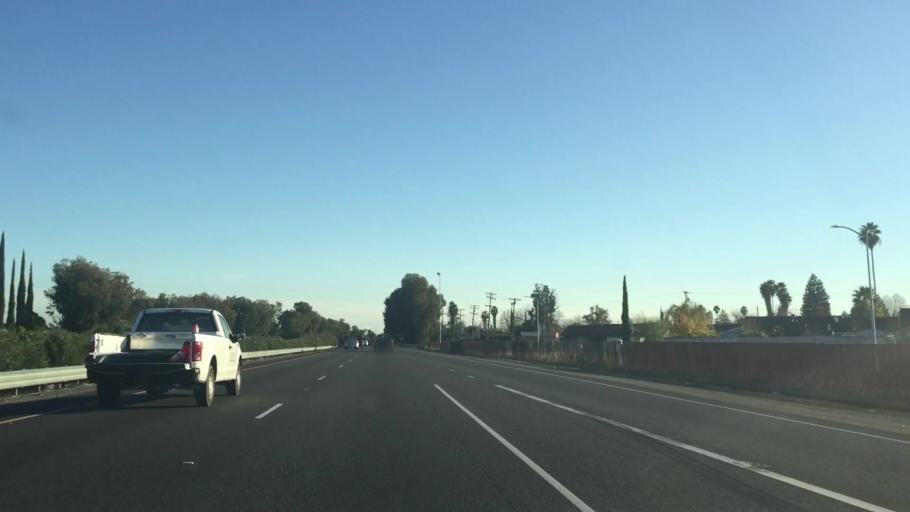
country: US
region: California
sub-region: Yuba County
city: Olivehurst
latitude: 39.1110
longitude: -121.5576
